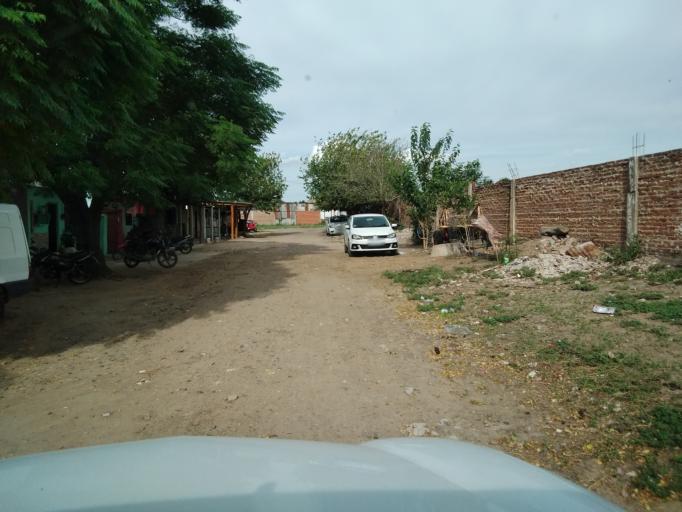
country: AR
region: Corrientes
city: Corrientes
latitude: -27.4824
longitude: -58.8514
